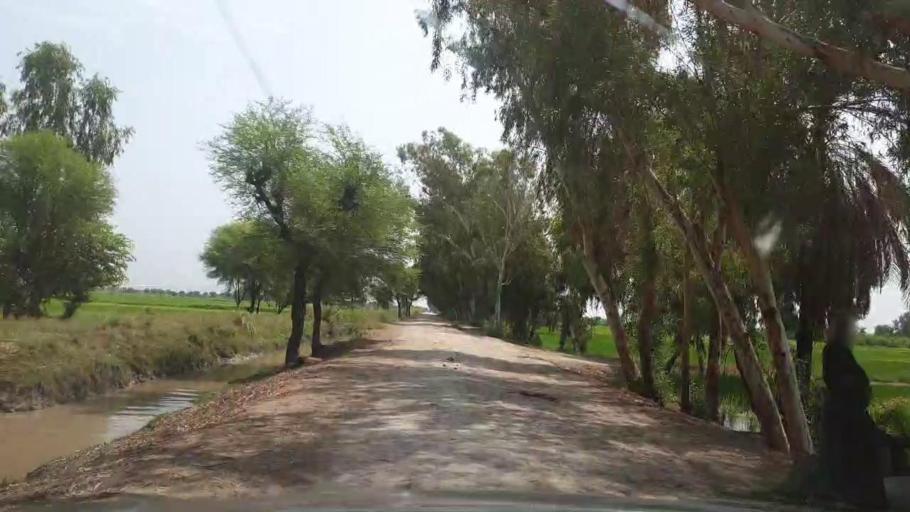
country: PK
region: Sindh
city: Ratodero
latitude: 27.8797
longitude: 68.3352
